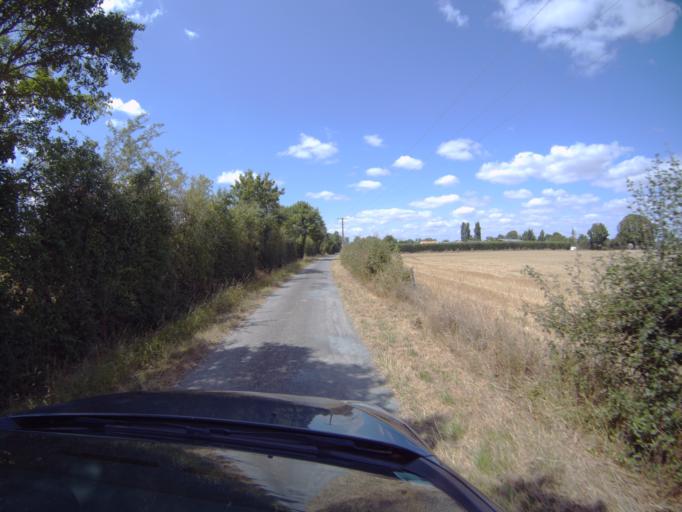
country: FR
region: Poitou-Charentes
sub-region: Departement des Deux-Sevres
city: Saint-Hilaire-la-Palud
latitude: 46.2738
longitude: -0.6526
